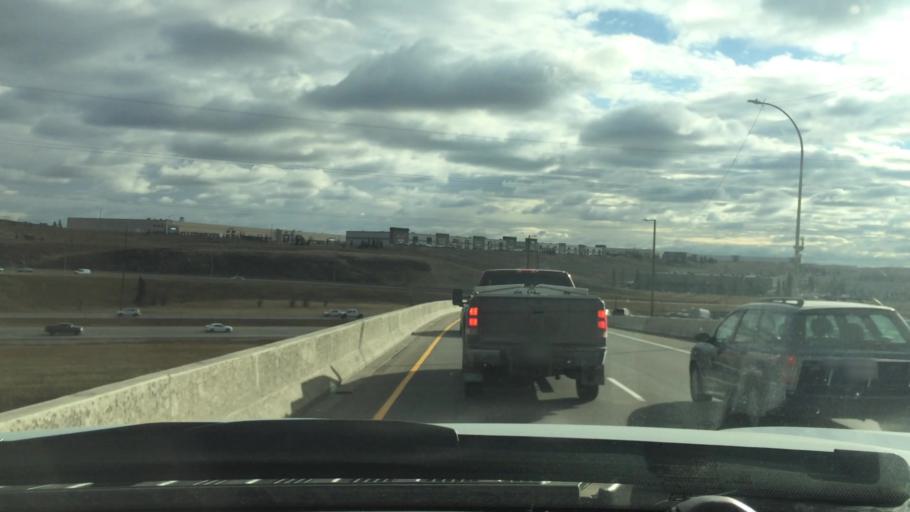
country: CA
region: Alberta
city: Calgary
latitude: 51.1254
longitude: -114.0484
